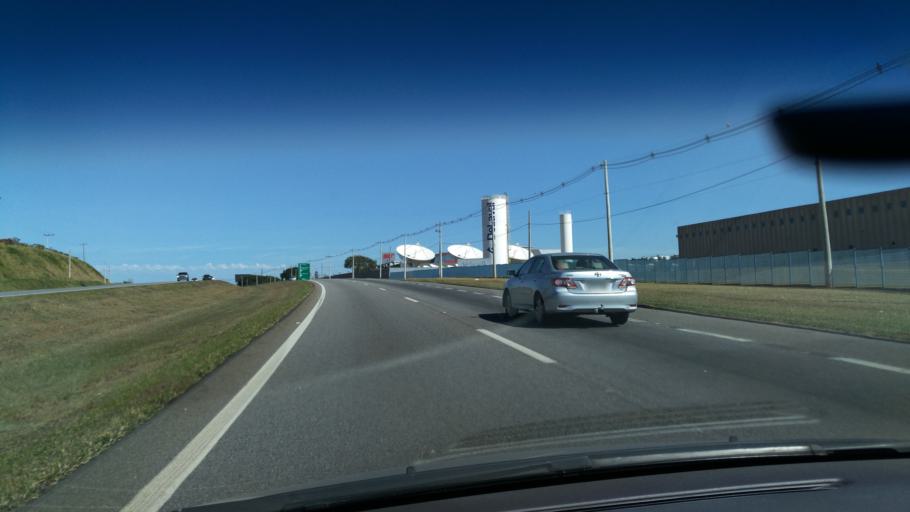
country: BR
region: Sao Paulo
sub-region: Jaguariuna
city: Jaguariuna
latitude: -22.6878
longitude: -47.0114
